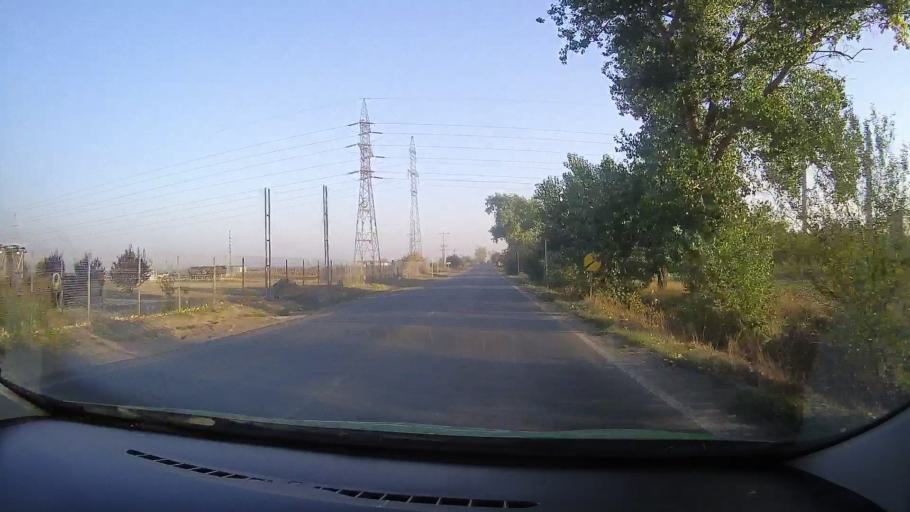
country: RO
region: Arad
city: Arad
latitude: 46.2179
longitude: 21.3205
